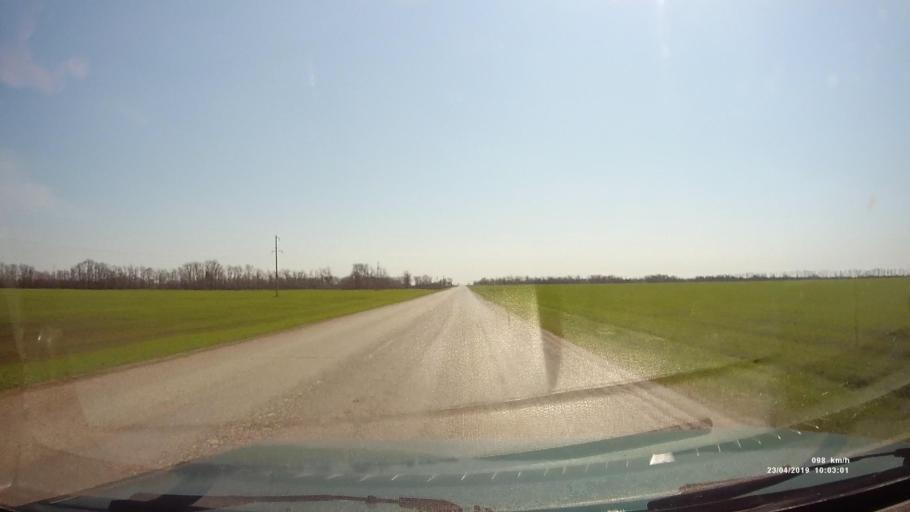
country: RU
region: Rostov
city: Sovetskoye
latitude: 46.7570
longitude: 42.1833
